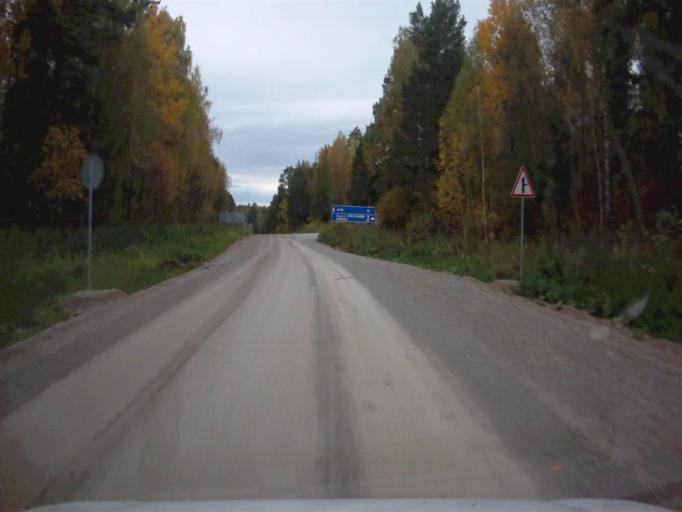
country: RU
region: Chelyabinsk
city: Nyazepetrovsk
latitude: 56.0859
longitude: 59.4189
